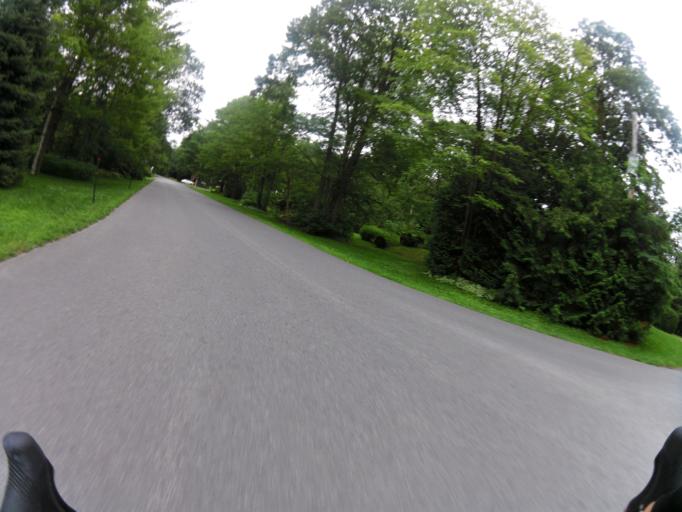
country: CA
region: Ontario
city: Ottawa
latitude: 45.3244
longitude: -75.7106
